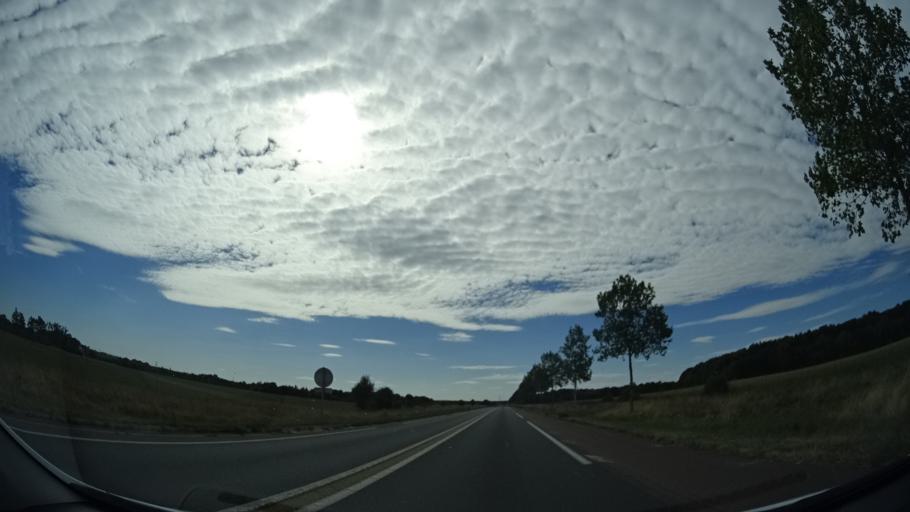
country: FR
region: Centre
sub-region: Departement du Loiret
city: Bellegarde
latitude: 47.9743
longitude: 2.4515
